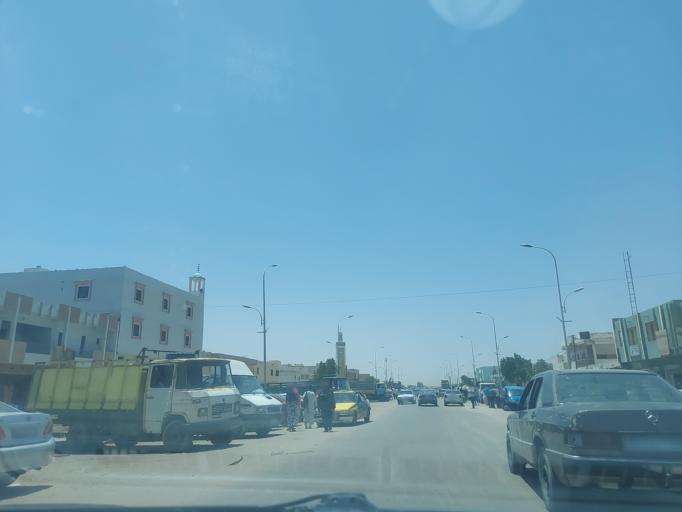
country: MR
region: Nouakchott
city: Nouakchott
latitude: 18.0810
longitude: -15.9816
